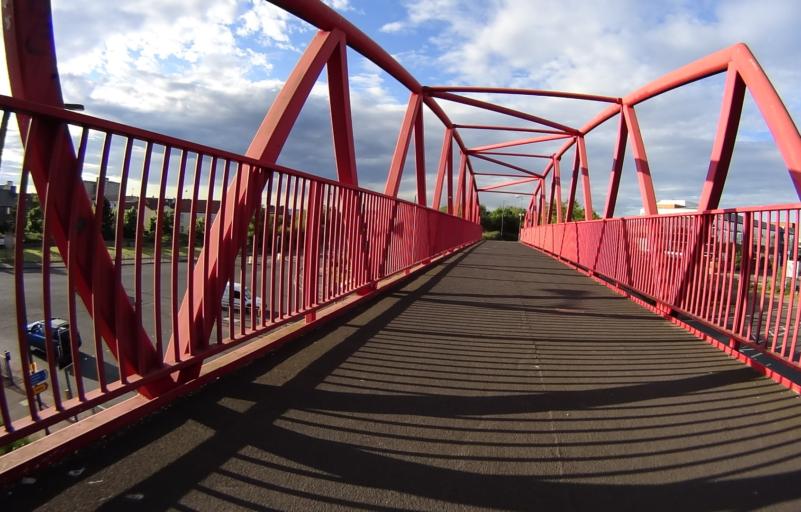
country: GB
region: Scotland
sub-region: Edinburgh
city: Edinburgh
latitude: 55.9683
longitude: -3.2396
